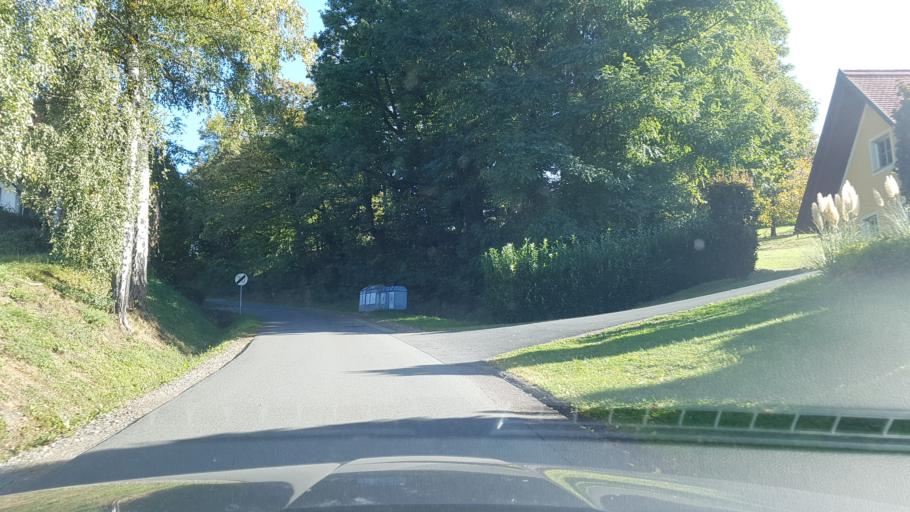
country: AT
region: Styria
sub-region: Politischer Bezirk Leibnitz
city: Kitzeck im Sausal
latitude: 46.7731
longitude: 15.4142
